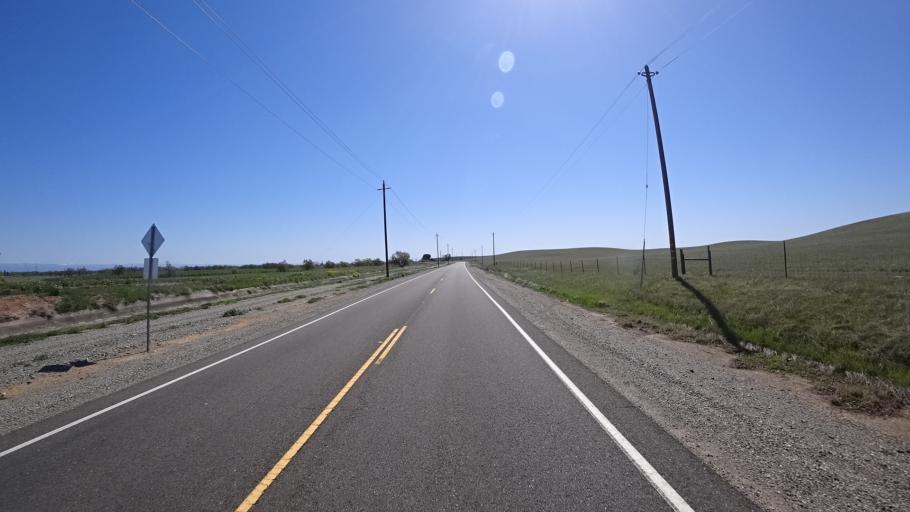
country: US
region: California
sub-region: Glenn County
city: Orland
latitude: 39.7865
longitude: -122.3014
